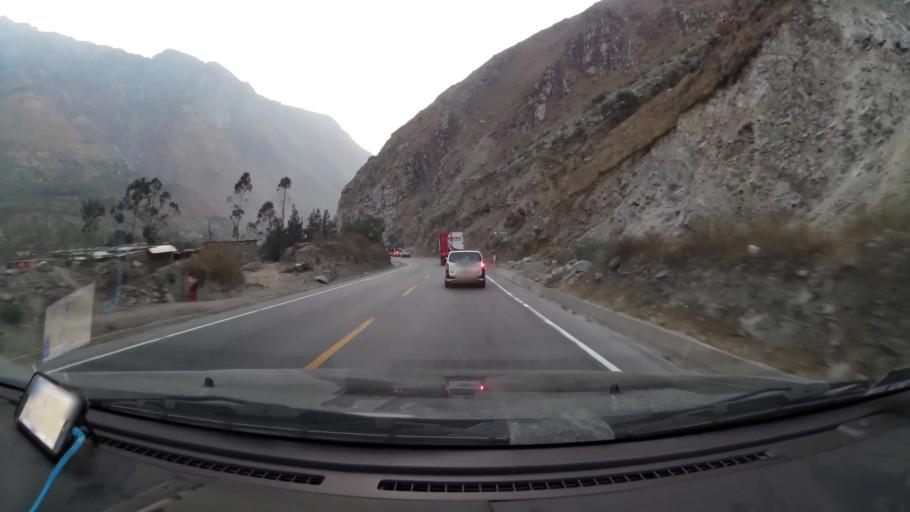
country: PE
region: Lima
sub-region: Provincia de Huarochiri
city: Surco
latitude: -11.8822
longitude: -76.4411
